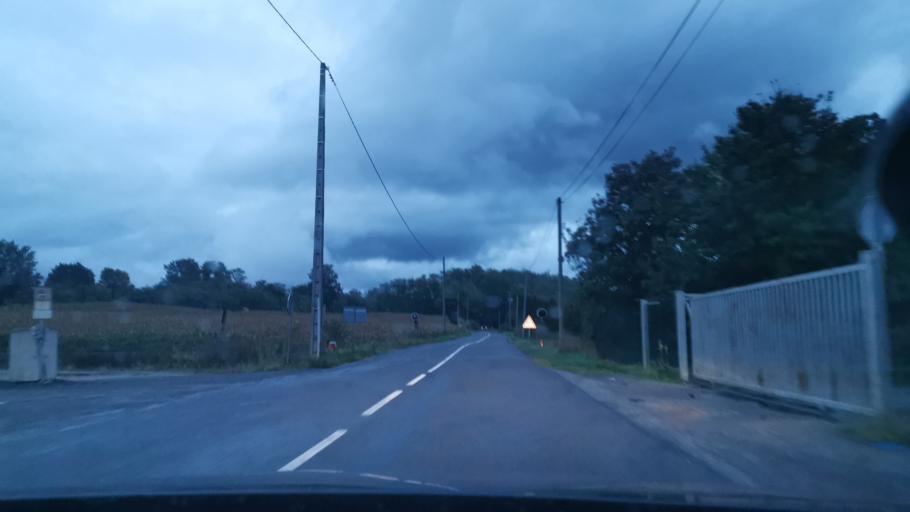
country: FR
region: Rhone-Alpes
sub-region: Departement de l'Ain
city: Pont-de-Veyle
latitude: 46.2658
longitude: 4.8944
